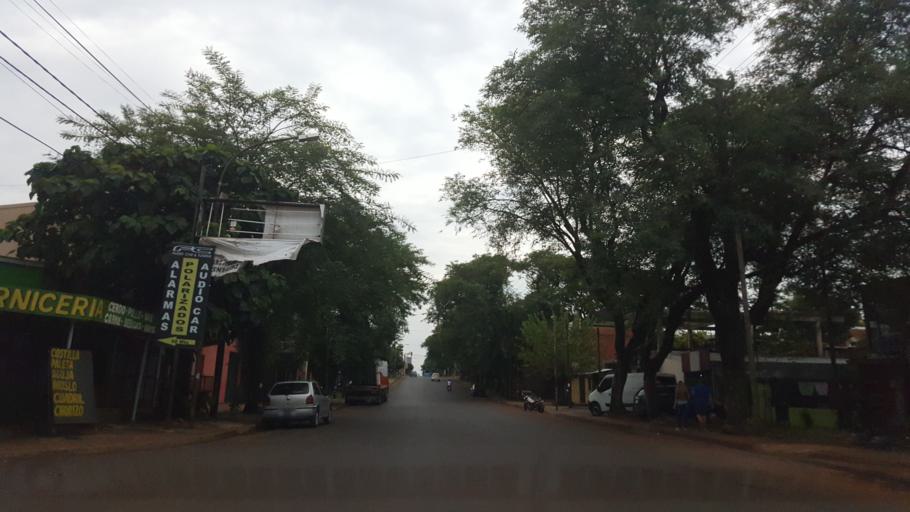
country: AR
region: Misiones
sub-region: Departamento de Capital
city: Posadas
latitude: -27.4033
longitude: -55.8988
